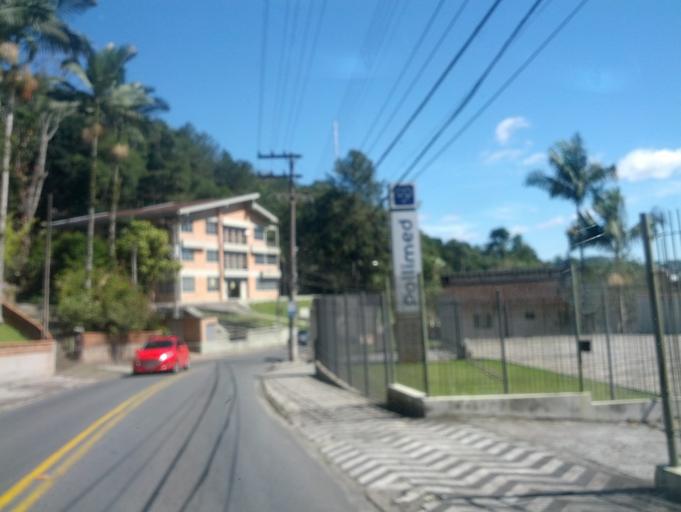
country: BR
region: Santa Catarina
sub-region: Blumenau
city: Blumenau
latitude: -26.9230
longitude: -49.0848
